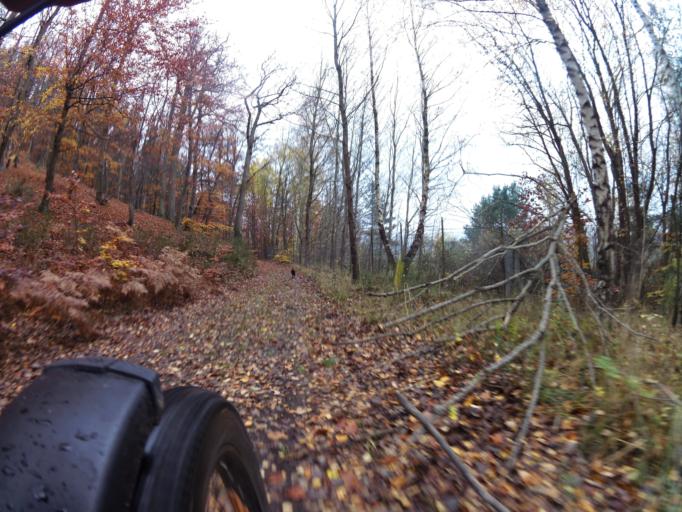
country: PL
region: Pomeranian Voivodeship
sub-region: Powiat wejherowski
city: Gniewino
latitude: 54.7521
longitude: 18.0855
